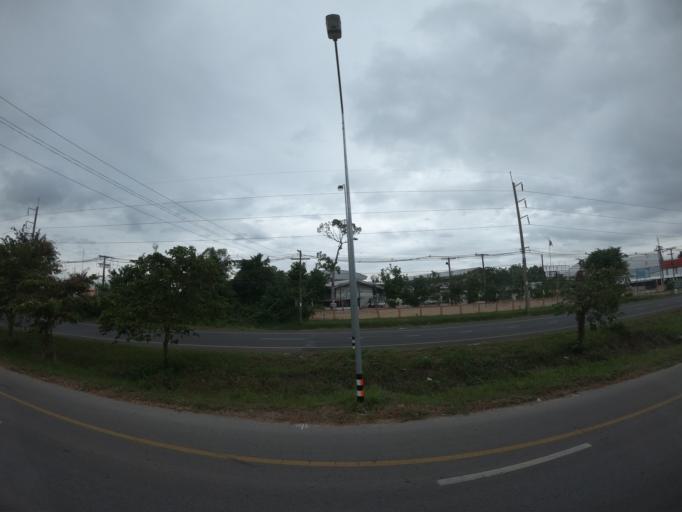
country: TH
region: Roi Et
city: Roi Et
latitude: 16.0443
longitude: 103.6282
